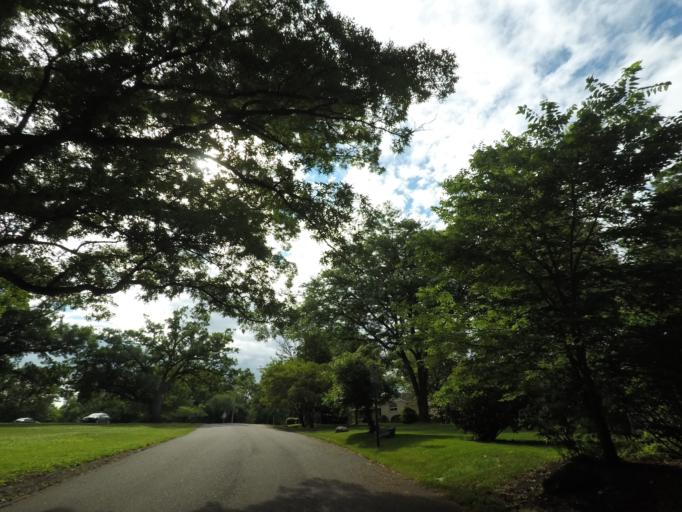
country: US
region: Wisconsin
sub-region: Rock County
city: Janesville
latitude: 42.6798
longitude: -88.9945
